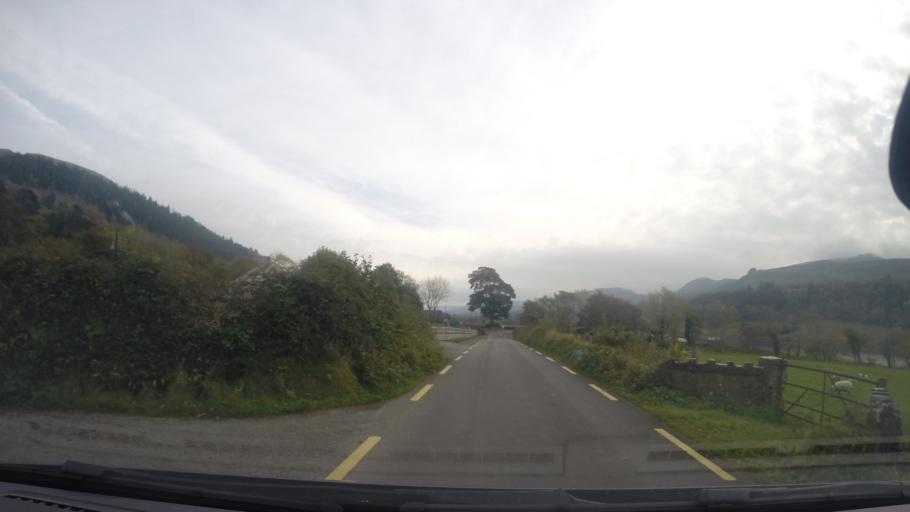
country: IE
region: Connaught
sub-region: Sligo
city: Sligo
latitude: 54.3393
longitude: -8.3708
